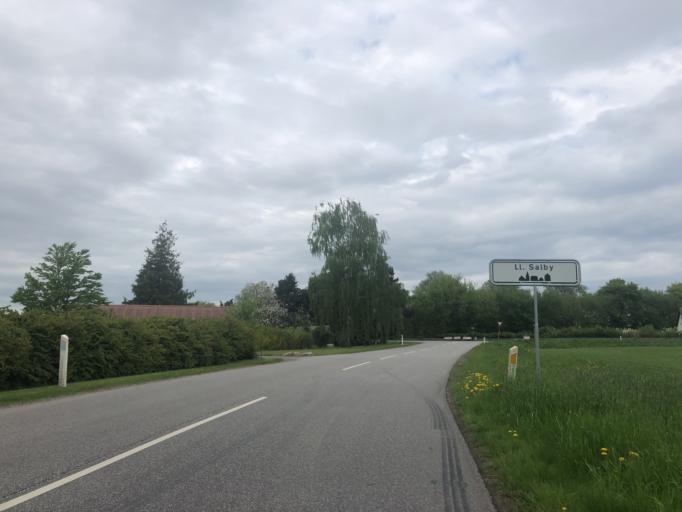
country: DK
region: Zealand
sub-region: Koge Kommune
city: Ejby
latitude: 55.4736
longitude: 12.1134
